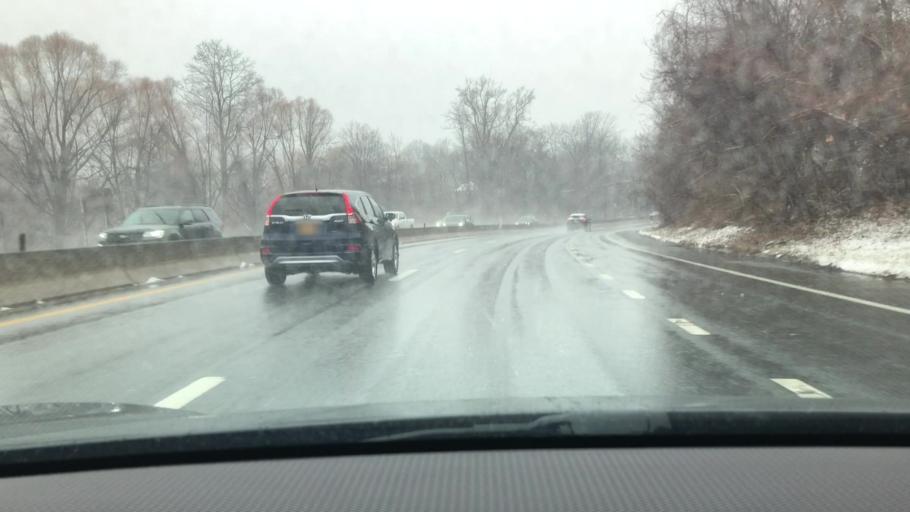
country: US
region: New York
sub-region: Westchester County
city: Tuckahoe
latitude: 40.9537
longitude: -73.7991
